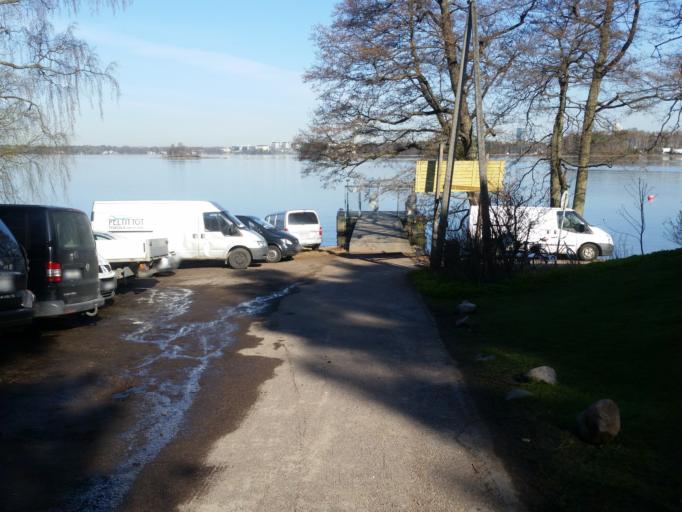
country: FI
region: Uusimaa
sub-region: Helsinki
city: Teekkarikylae
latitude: 60.1562
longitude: 24.8560
